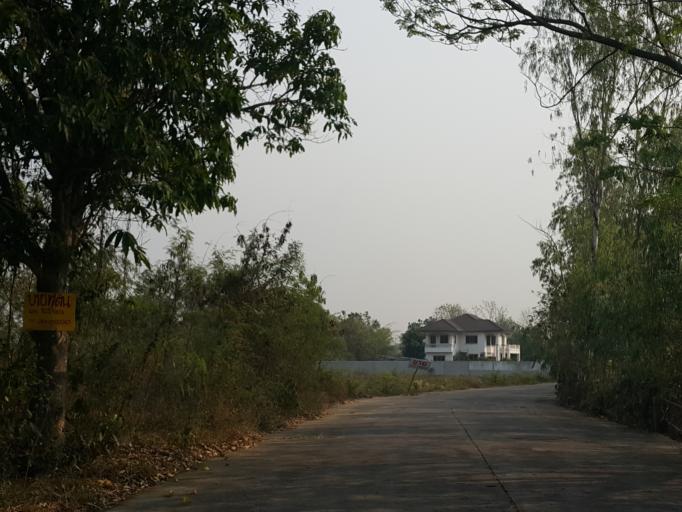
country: TH
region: Chiang Mai
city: San Kamphaeng
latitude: 18.7545
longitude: 99.1050
